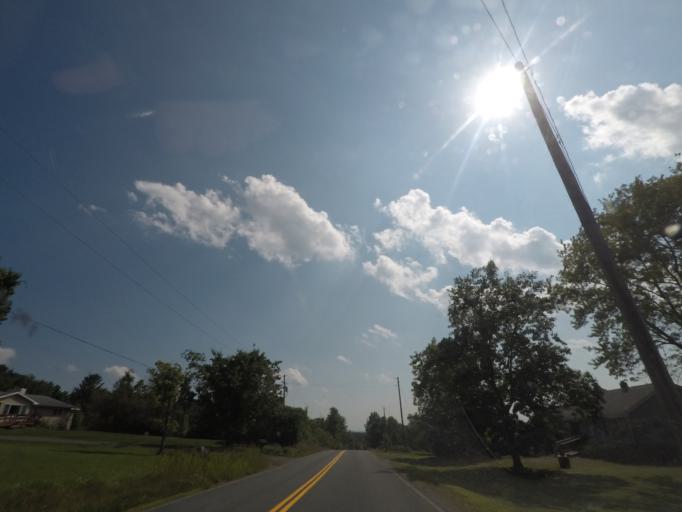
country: US
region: New York
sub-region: Rensselaer County
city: Averill Park
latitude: 42.6491
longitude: -73.5263
